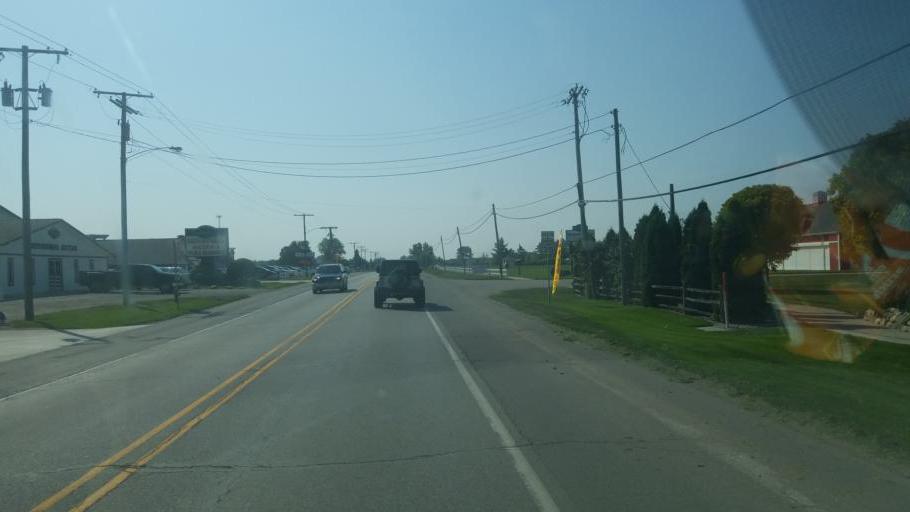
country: US
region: Indiana
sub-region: Elkhart County
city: Middlebury
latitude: 41.6737
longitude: -85.5806
